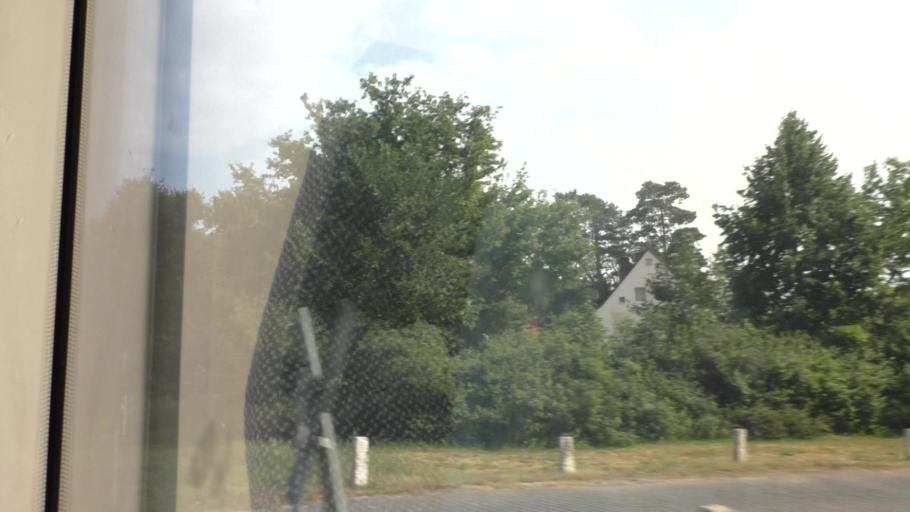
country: DE
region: Brandenburg
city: Konigs Wusterhausen
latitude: 52.3009
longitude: 13.7108
